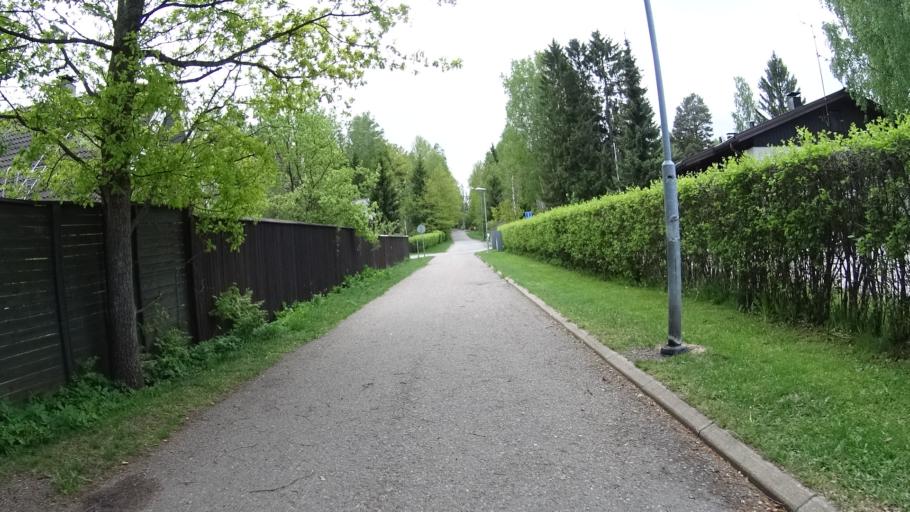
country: FI
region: Uusimaa
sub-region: Helsinki
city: Kauniainen
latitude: 60.2305
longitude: 24.7208
